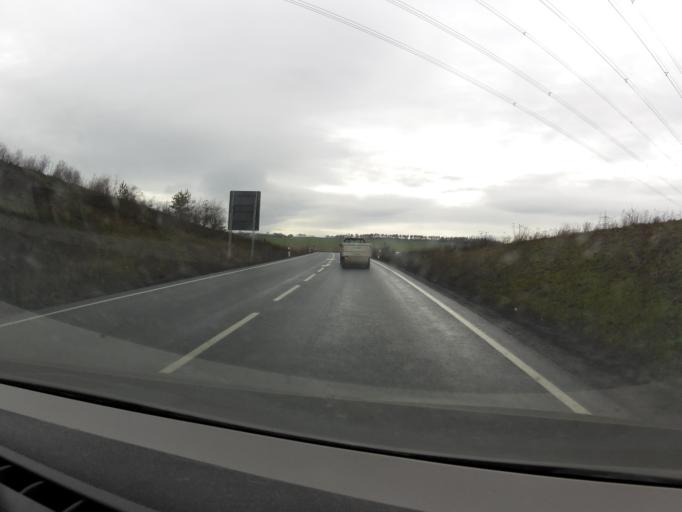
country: DE
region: Saxony-Anhalt
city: Grossorner
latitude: 51.6110
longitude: 11.4754
